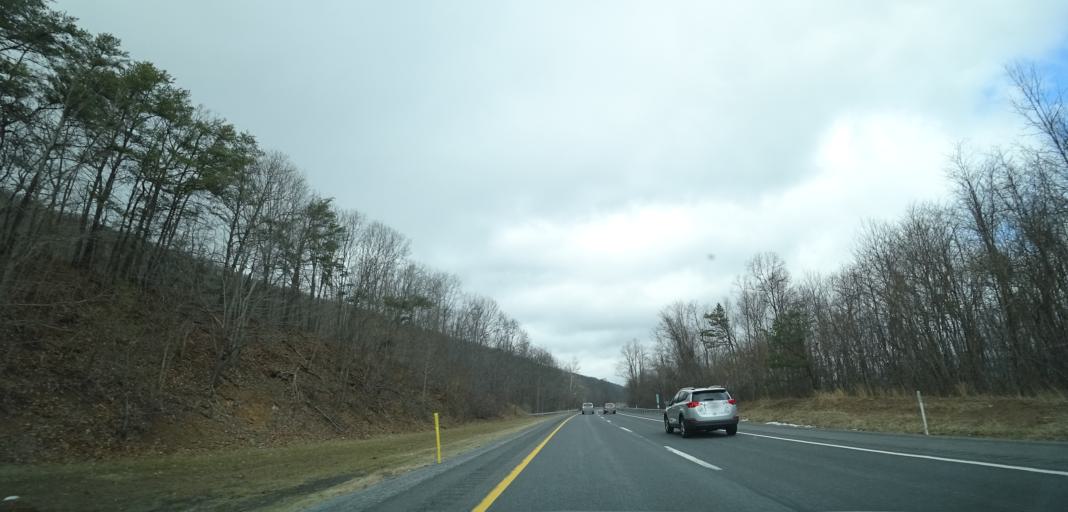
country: US
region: Maryland
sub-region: Washington County
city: Hancock
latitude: 39.8418
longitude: -78.2755
